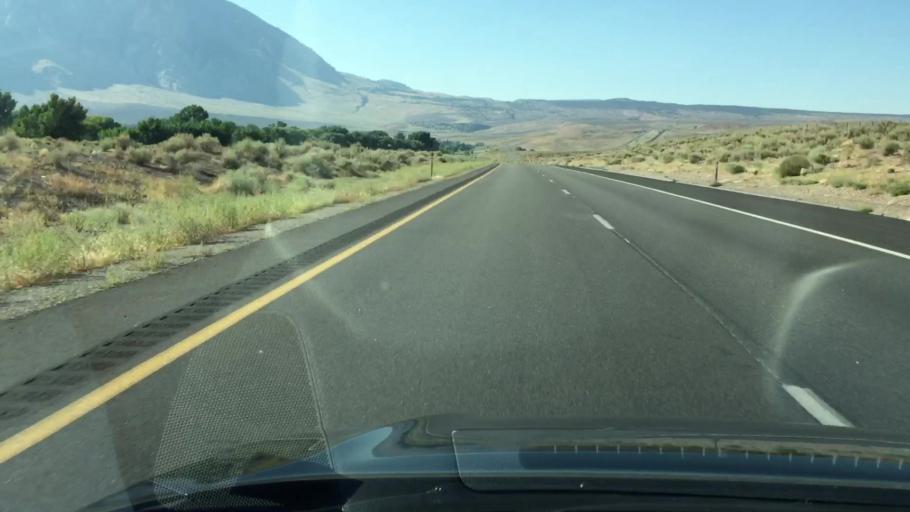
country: US
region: California
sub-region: Inyo County
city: West Bishop
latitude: 37.4257
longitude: -118.5591
